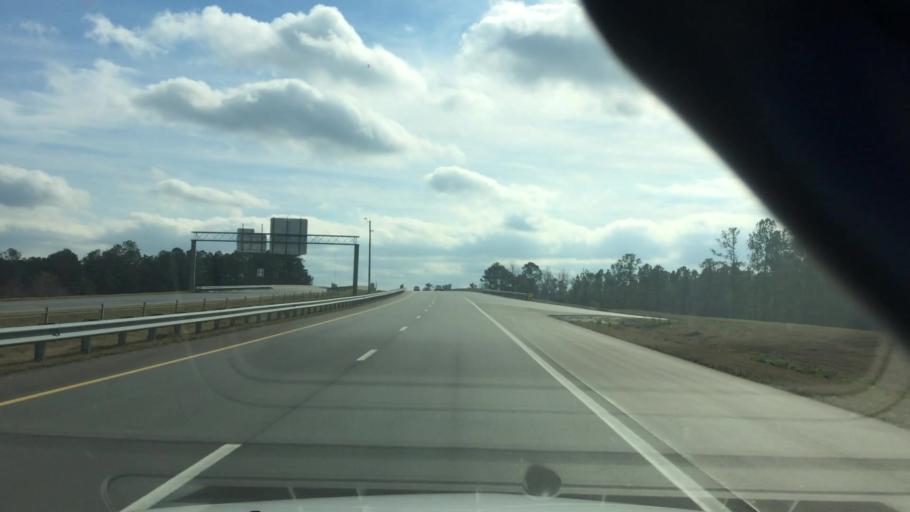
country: US
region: North Carolina
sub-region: Brunswick County
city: Leland
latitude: 34.2603
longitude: -78.0801
